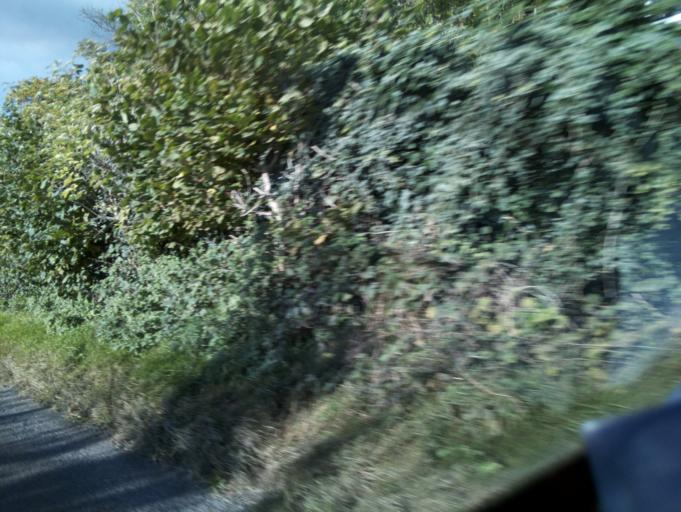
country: GB
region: England
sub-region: Herefordshire
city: Kinnersley
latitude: 52.1054
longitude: -2.9561
